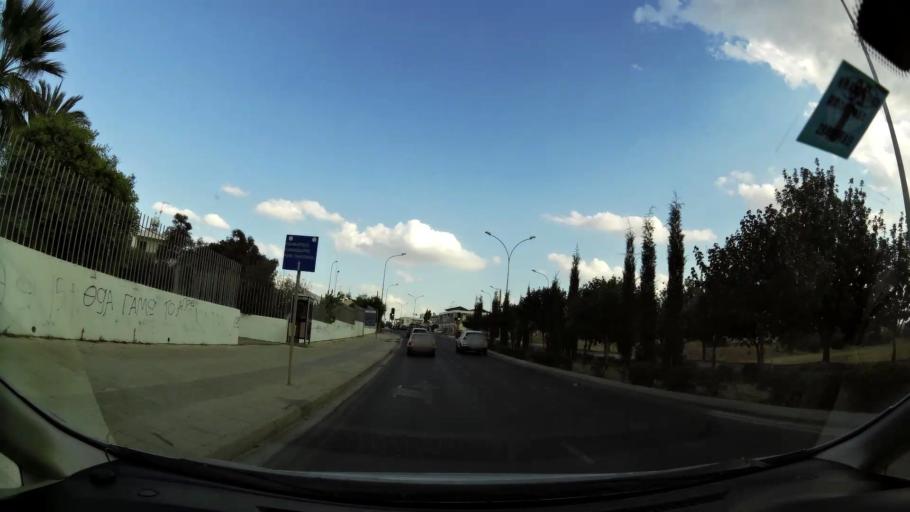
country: CY
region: Lefkosia
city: Kato Deftera
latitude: 35.1098
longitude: 33.2963
